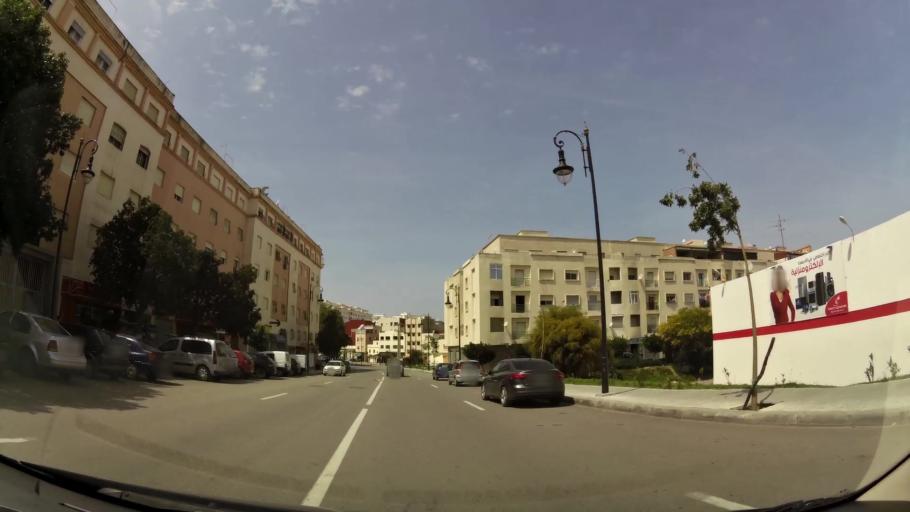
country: MA
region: Tanger-Tetouan
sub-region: Tanger-Assilah
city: Tangier
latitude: 35.7453
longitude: -5.8470
